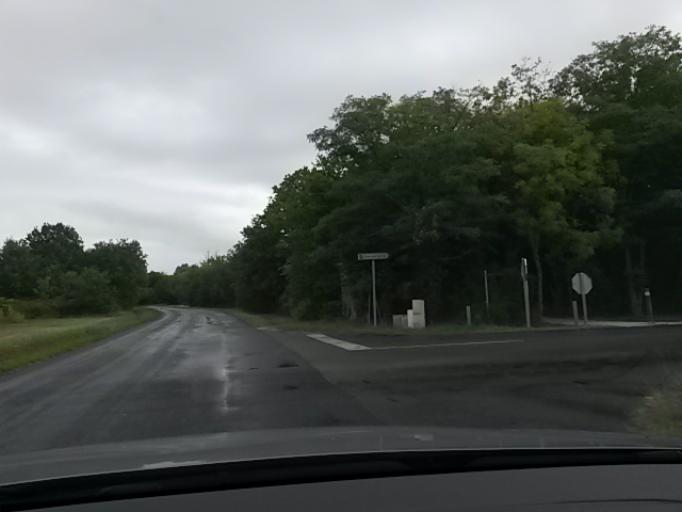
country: FR
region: Poitou-Charentes
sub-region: Departement de la Charente-Maritime
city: Dolus-d'Oleron
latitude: 45.8858
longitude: -1.2410
